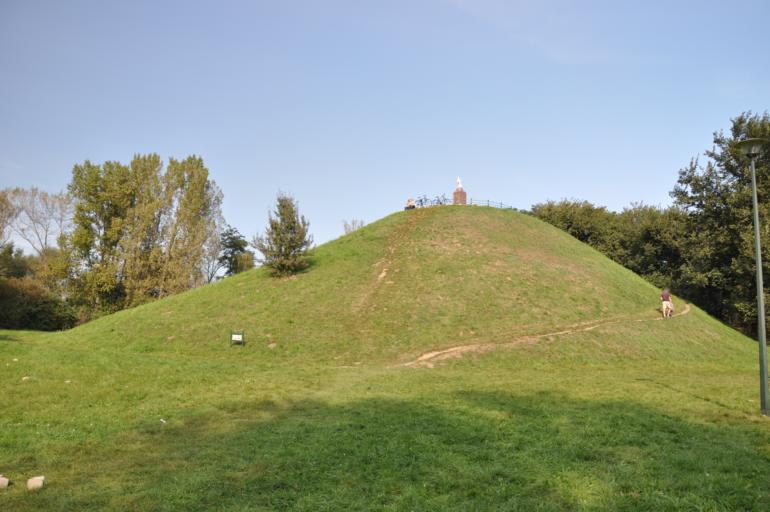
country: PL
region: Lesser Poland Voivodeship
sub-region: Powiat wielicki
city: Kokotow
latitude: 50.0702
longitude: 20.0681
